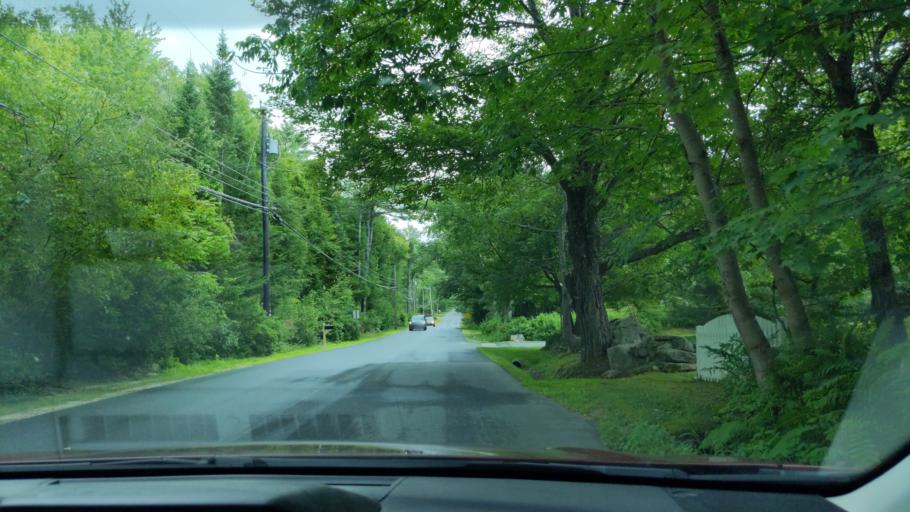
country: US
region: New Hampshire
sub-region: Merrimack County
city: New London
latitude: 43.4144
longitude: -72.0107
